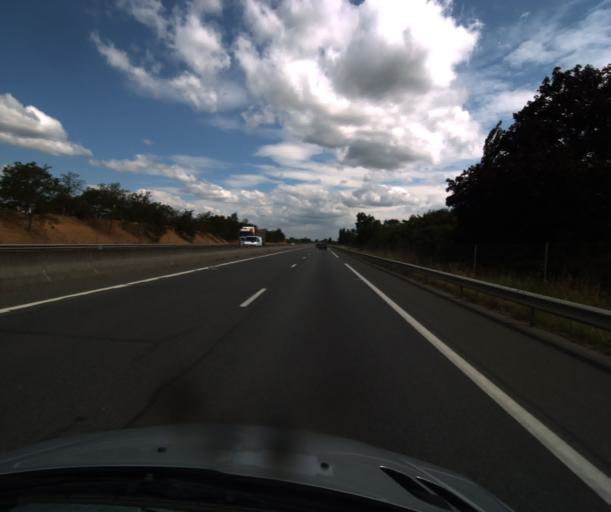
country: FR
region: Midi-Pyrenees
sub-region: Departement du Tarn-et-Garonne
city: Bressols
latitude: 43.9628
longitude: 1.3293
